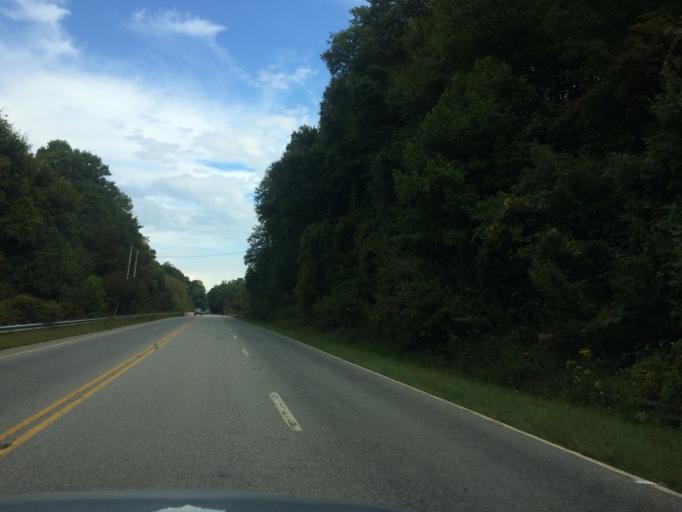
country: US
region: North Carolina
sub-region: Haywood County
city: Canton
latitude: 35.5386
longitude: -82.7712
